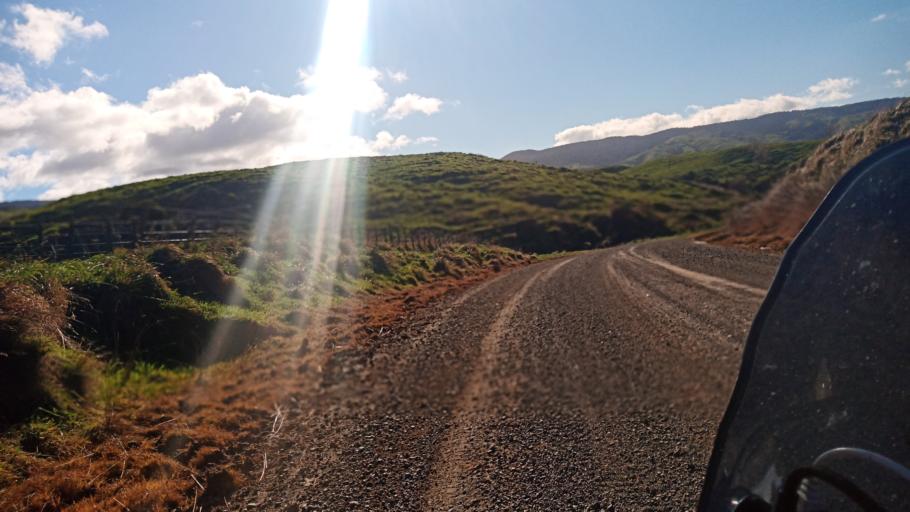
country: NZ
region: Hawke's Bay
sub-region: Wairoa District
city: Wairoa
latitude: -38.7473
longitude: 177.2795
